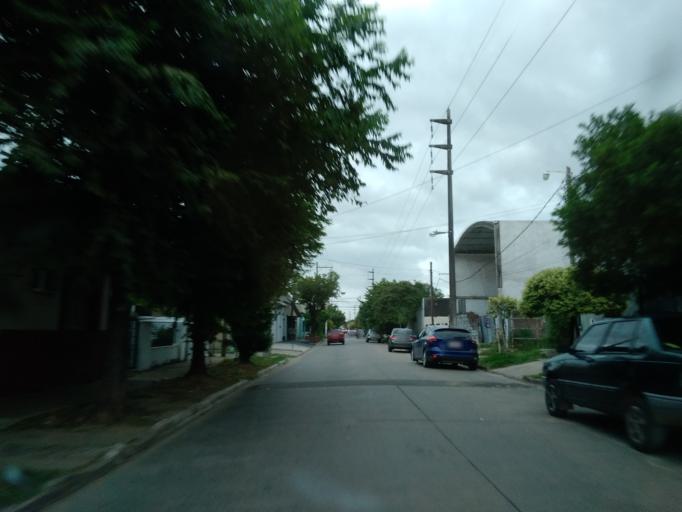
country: AR
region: Corrientes
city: Corrientes
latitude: -27.4797
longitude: -58.8246
